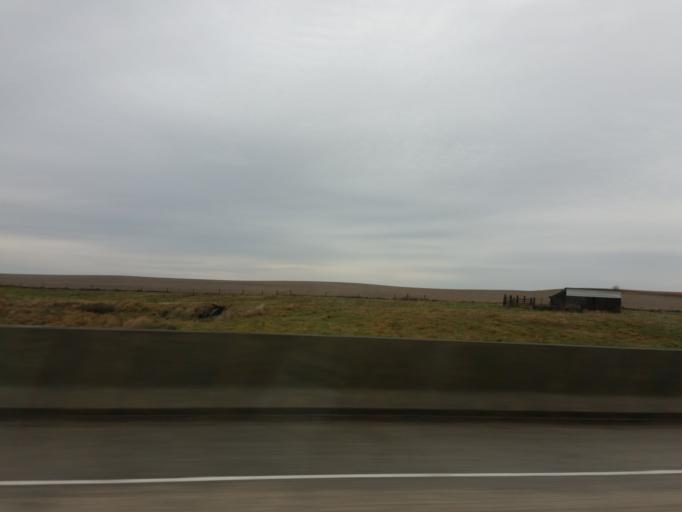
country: US
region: Iowa
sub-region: Benton County
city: Vinton
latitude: 42.0371
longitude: -92.0289
